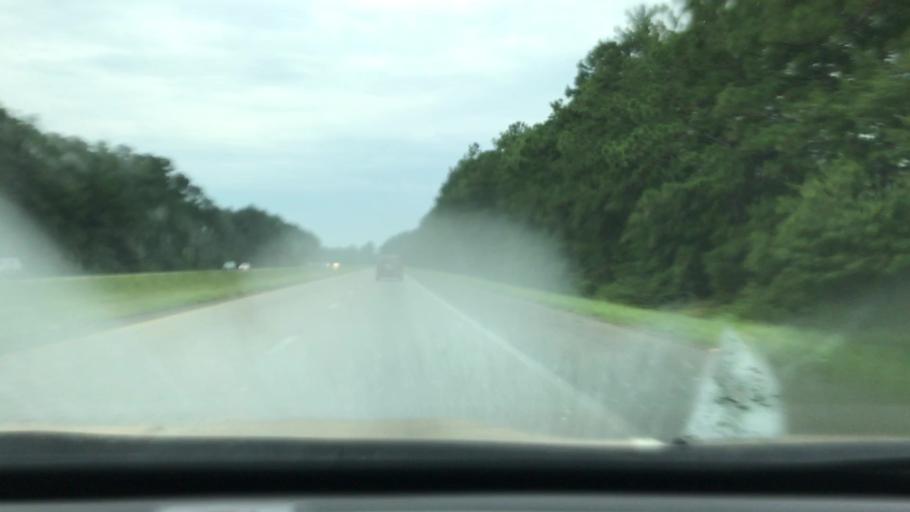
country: US
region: South Carolina
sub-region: Colleton County
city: Walterboro
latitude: 32.8141
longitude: -80.7621
